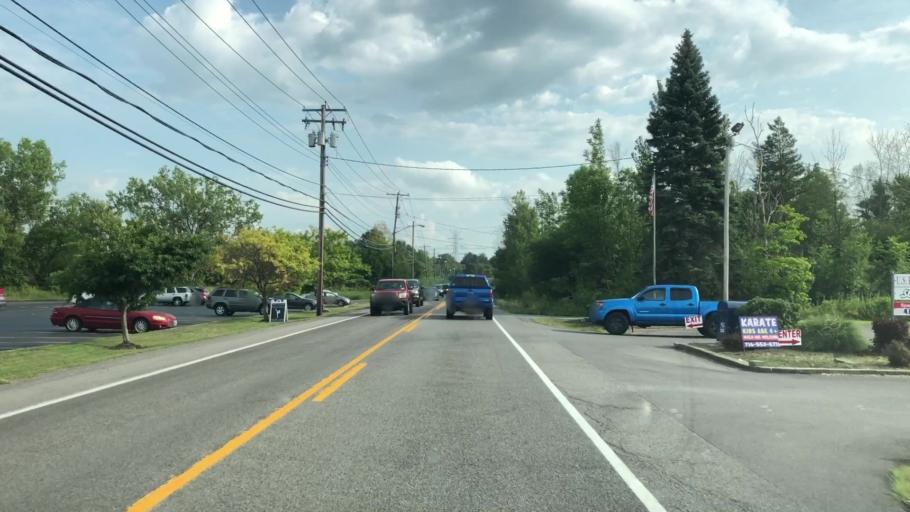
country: US
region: New York
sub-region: Erie County
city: Elma Center
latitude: 42.8350
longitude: -78.6368
